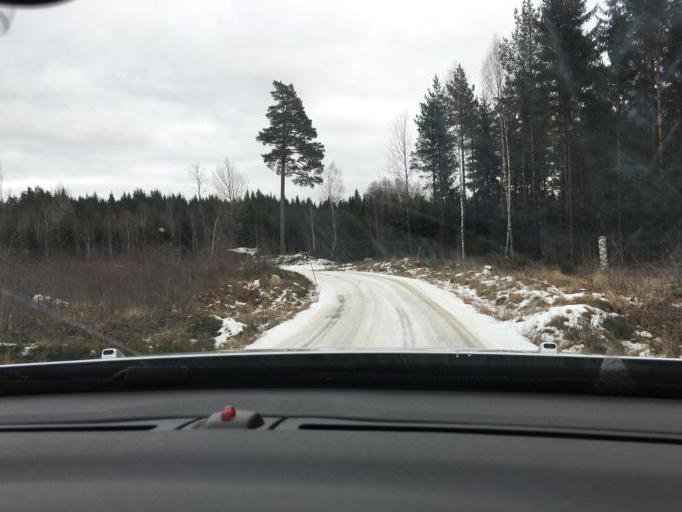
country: SE
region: Soedermanland
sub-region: Katrineholms Kommun
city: Katrineholm
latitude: 58.9974
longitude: 16.2905
